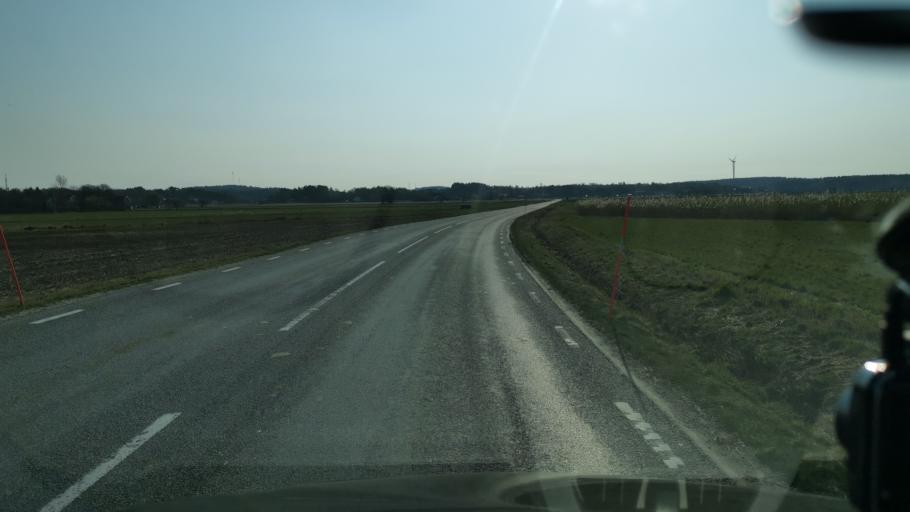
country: SE
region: Vaestra Goetaland
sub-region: Kungalvs Kommun
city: Kode
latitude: 57.9406
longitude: 11.8262
